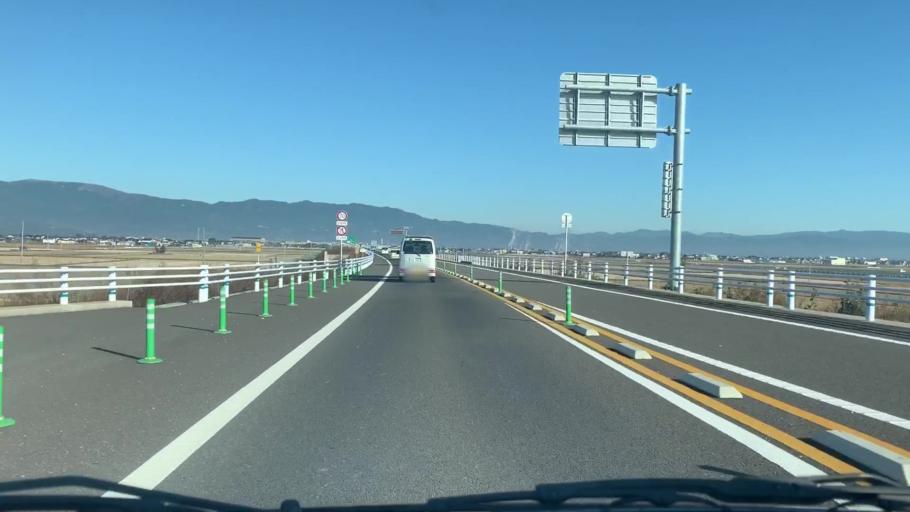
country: JP
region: Saga Prefecture
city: Saga-shi
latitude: 33.2062
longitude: 130.2151
